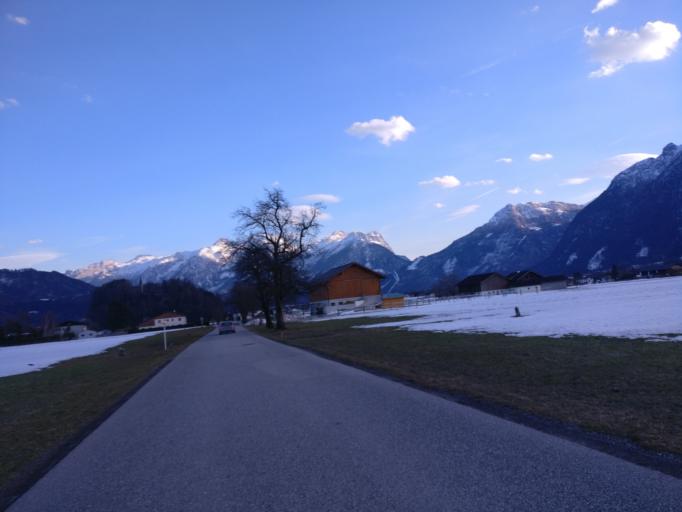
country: AT
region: Salzburg
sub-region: Politischer Bezirk Hallein
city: Kuchl
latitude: 47.6424
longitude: 13.1513
